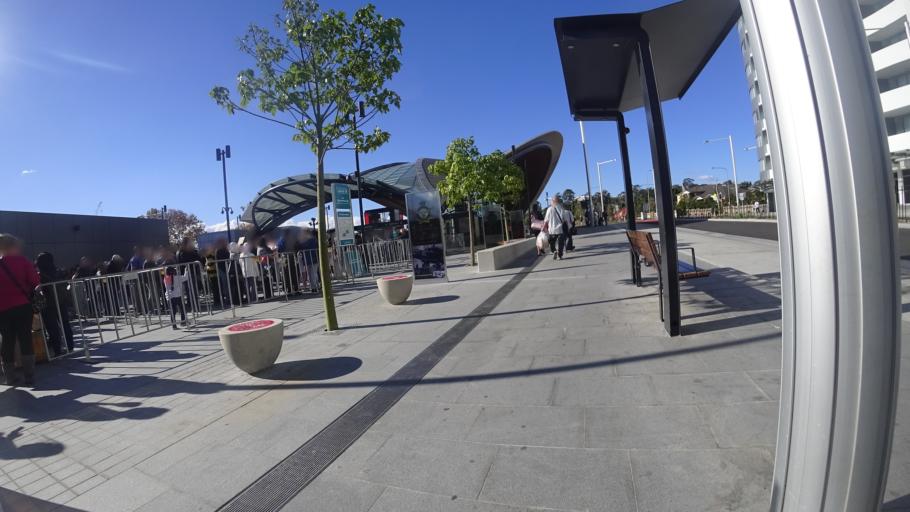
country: AU
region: New South Wales
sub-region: The Hills Shire
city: Castle Hill
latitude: -33.7319
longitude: 151.0069
